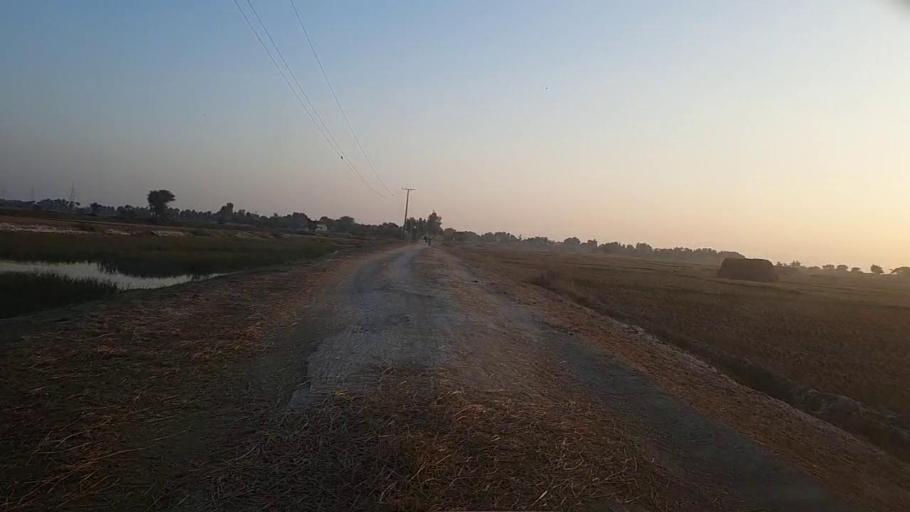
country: PK
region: Sindh
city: Khairpur Nathan Shah
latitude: 27.1622
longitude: 67.7321
